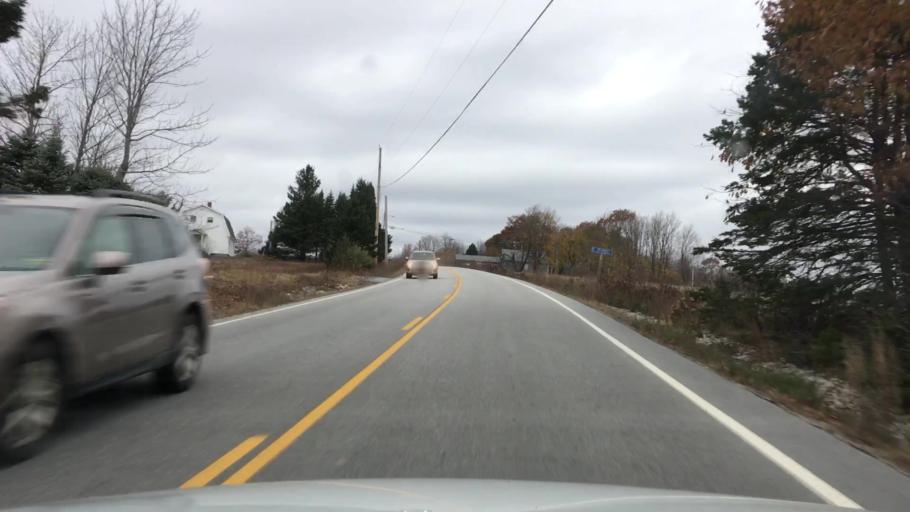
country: US
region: Maine
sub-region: Hancock County
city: Penobscot
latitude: 44.5189
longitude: -68.6591
